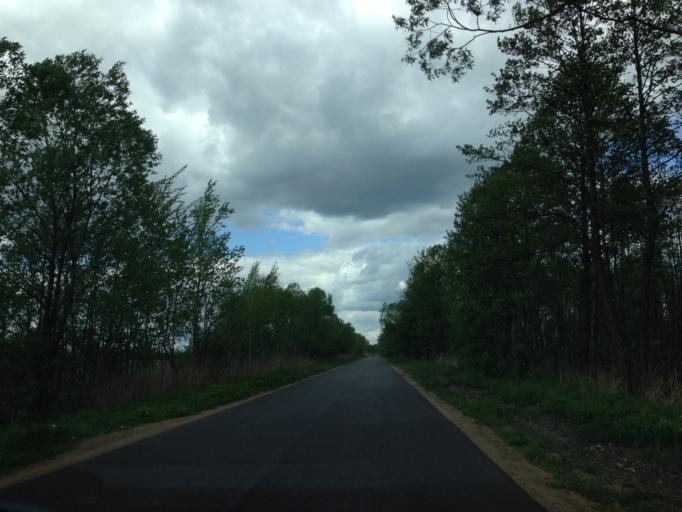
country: PL
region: Podlasie
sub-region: Powiat bialostocki
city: Tykocin
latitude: 53.2919
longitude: 22.6084
